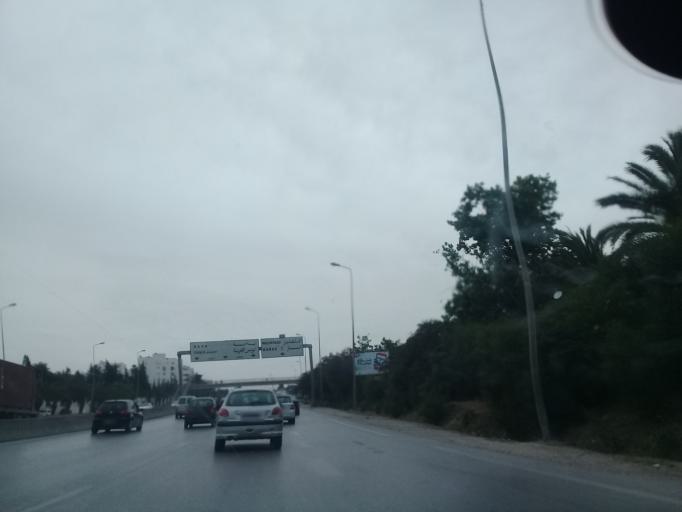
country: TN
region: Tunis
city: Tunis
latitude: 36.8371
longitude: 10.1629
